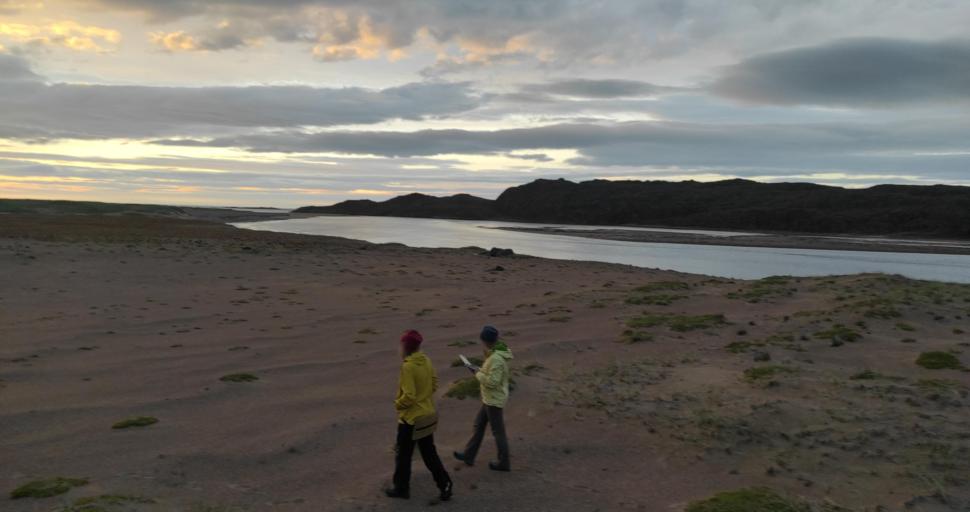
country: RU
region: Murmansk
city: Teriberka
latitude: 69.1670
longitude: 35.7973
